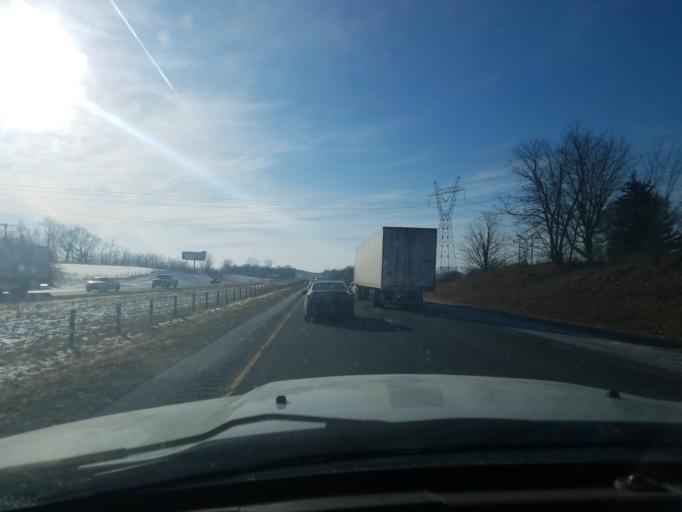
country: US
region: Indiana
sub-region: Madison County
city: Pendleton
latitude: 40.0422
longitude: -85.7067
